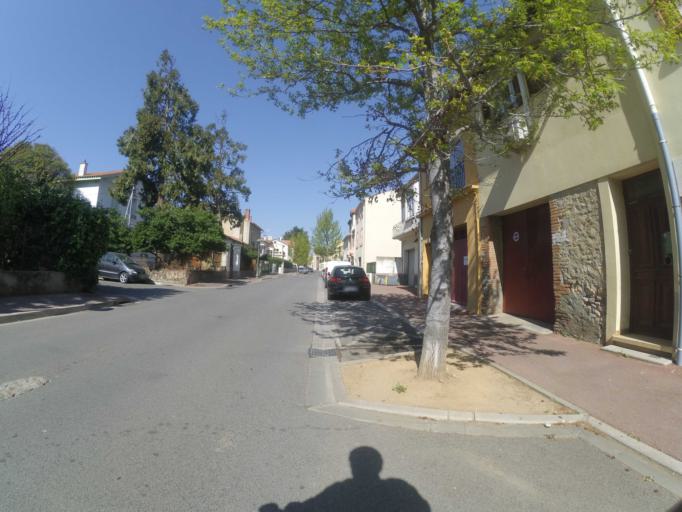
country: FR
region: Languedoc-Roussillon
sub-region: Departement des Pyrenees-Orientales
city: Thuir
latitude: 42.6304
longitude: 2.7583
